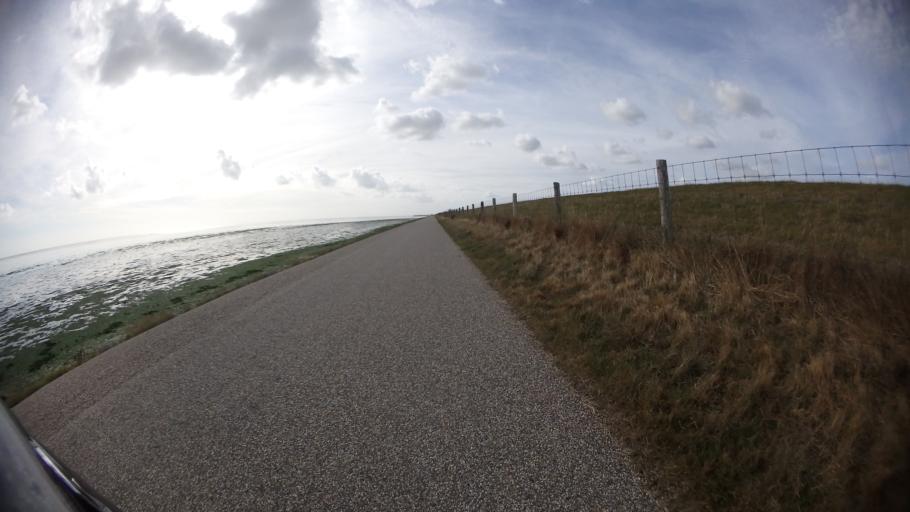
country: NL
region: North Holland
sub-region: Gemeente Texel
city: Den Burg
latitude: 53.1171
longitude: 4.8990
